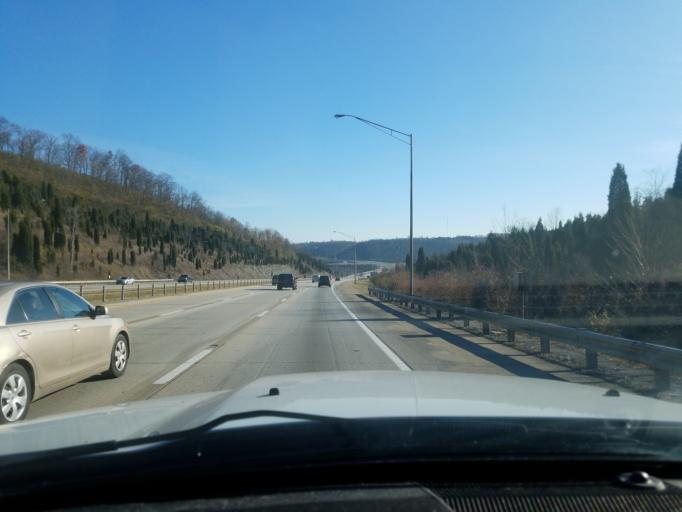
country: US
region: Kentucky
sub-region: Kenton County
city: Taylor Mill
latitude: 39.0224
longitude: -84.4992
